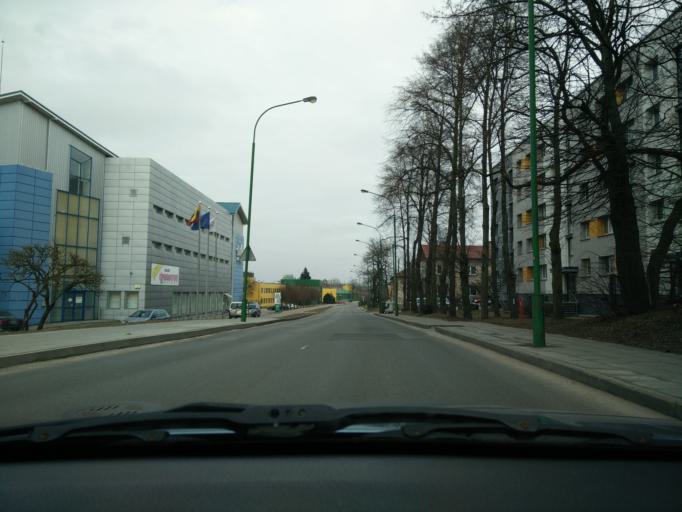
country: LT
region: Klaipedos apskritis
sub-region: Klaipeda
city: Klaipeda
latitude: 55.7125
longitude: 21.1512
